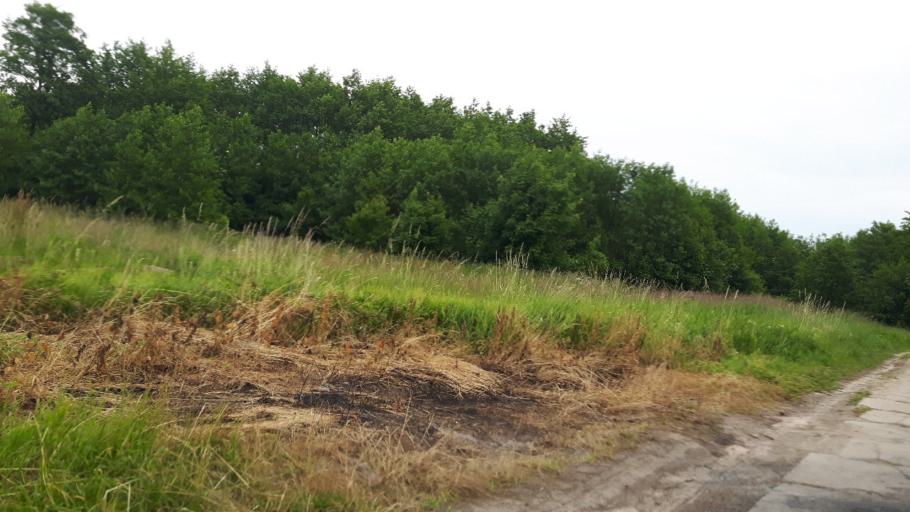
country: PL
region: Warmian-Masurian Voivodeship
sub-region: Powiat elblaski
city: Tolkmicko
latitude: 54.3265
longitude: 19.6045
